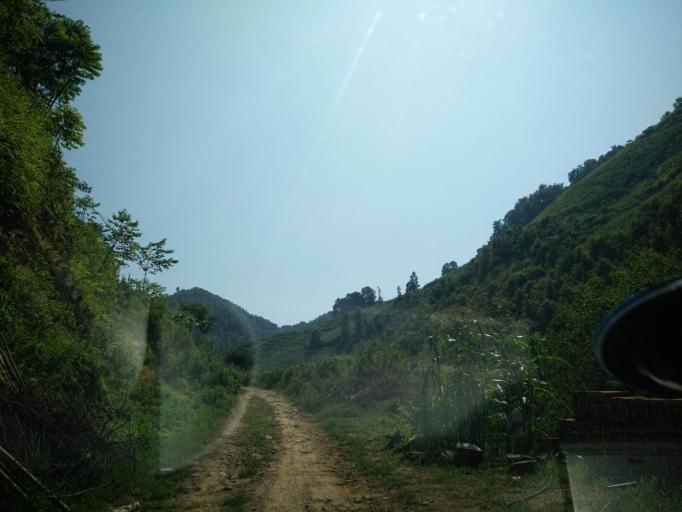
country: CN
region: Guangxi Zhuangzu Zizhiqu
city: Xinzhou
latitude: 25.1840
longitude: 105.6892
